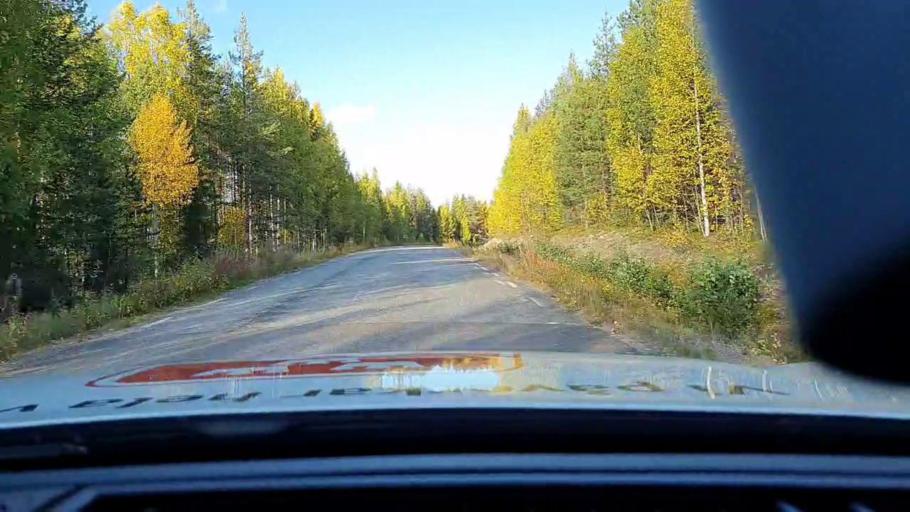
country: SE
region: Norrbotten
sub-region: Pitea Kommun
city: Norrfjarden
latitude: 65.6486
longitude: 21.4555
